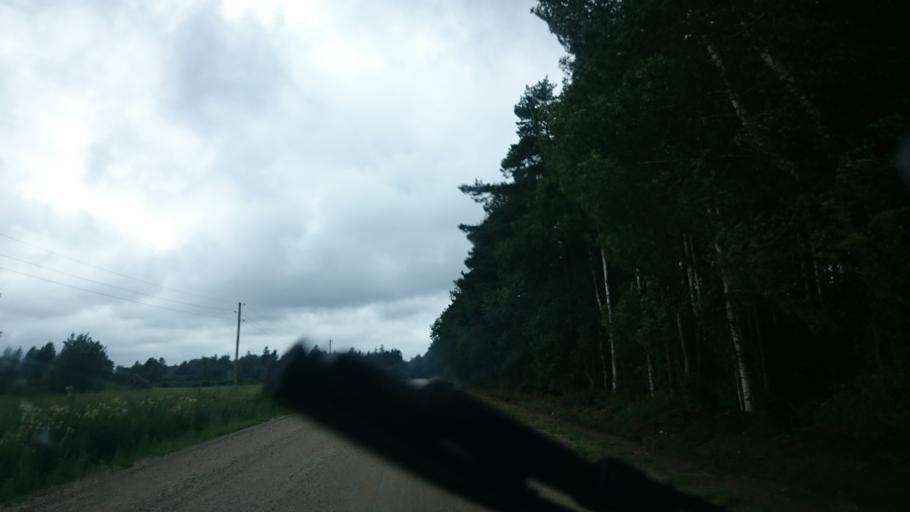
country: LV
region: Pavilostas
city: Pavilosta
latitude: 56.8543
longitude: 21.2428
